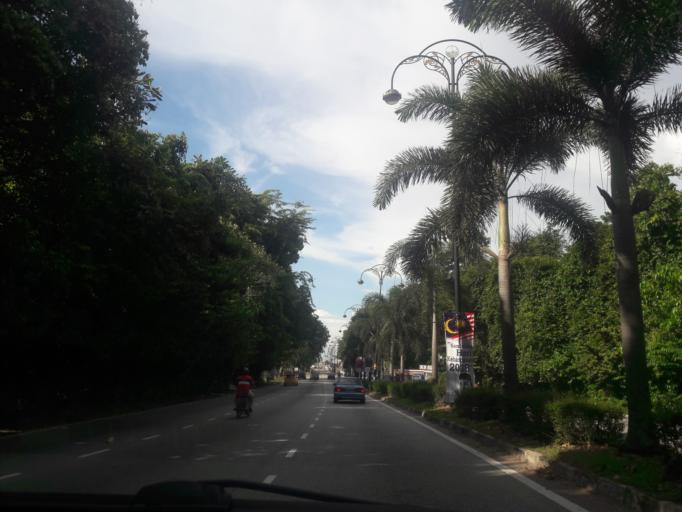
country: MY
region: Kedah
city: Sungai Petani
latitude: 5.6515
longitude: 100.4998
